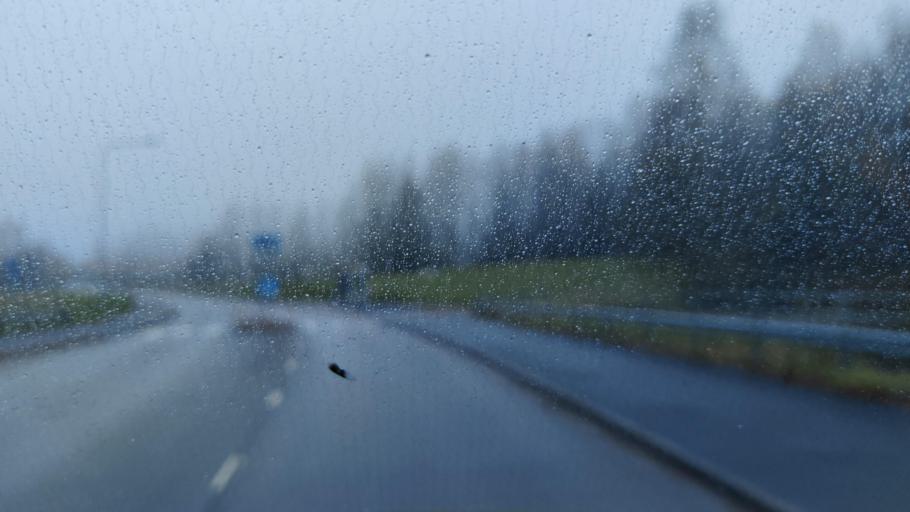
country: FI
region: Uusimaa
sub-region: Helsinki
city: Kerava
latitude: 60.3662
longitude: 25.0820
